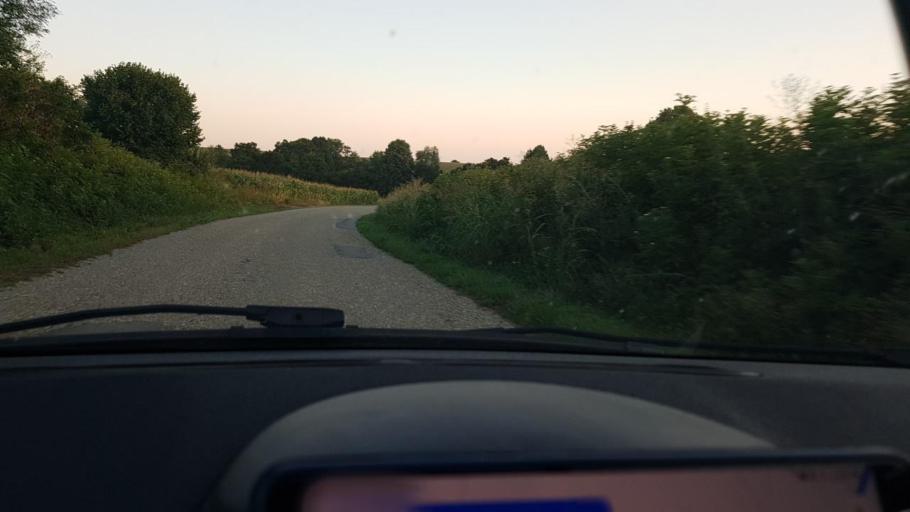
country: HR
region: Bjelovarsko-Bilogorska
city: Zdralovi
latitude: 45.8670
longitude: 17.0003
